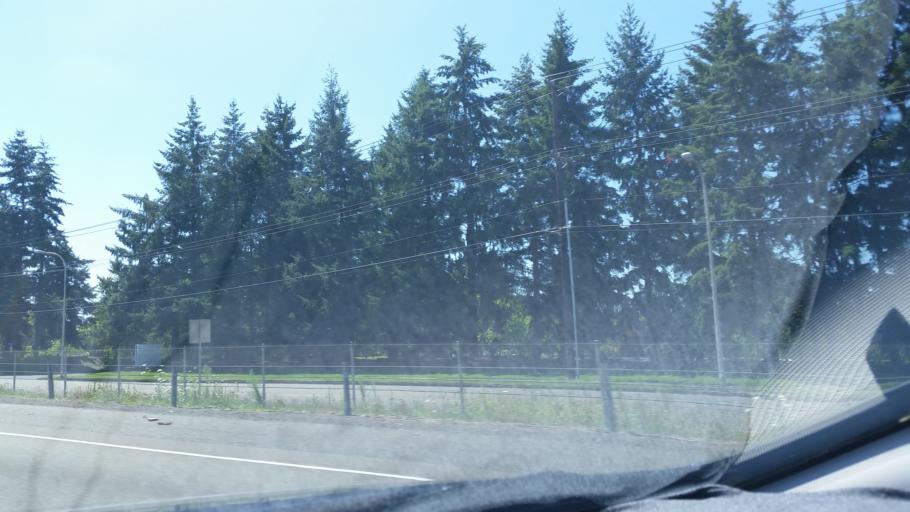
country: US
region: Oregon
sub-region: Clackamas County
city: Wilsonville
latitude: 45.3096
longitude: -122.7695
